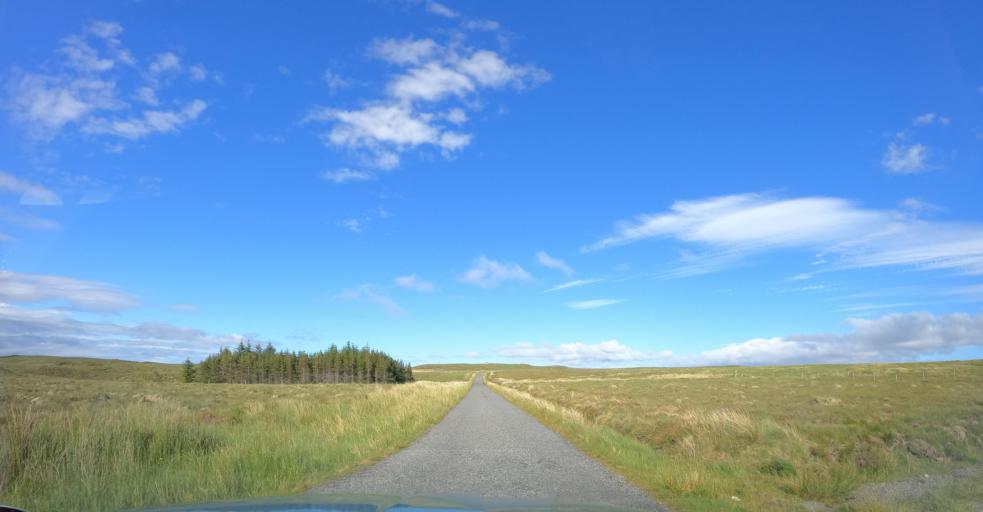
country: GB
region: Scotland
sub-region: Eilean Siar
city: Stornoway
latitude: 58.1795
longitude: -6.5464
